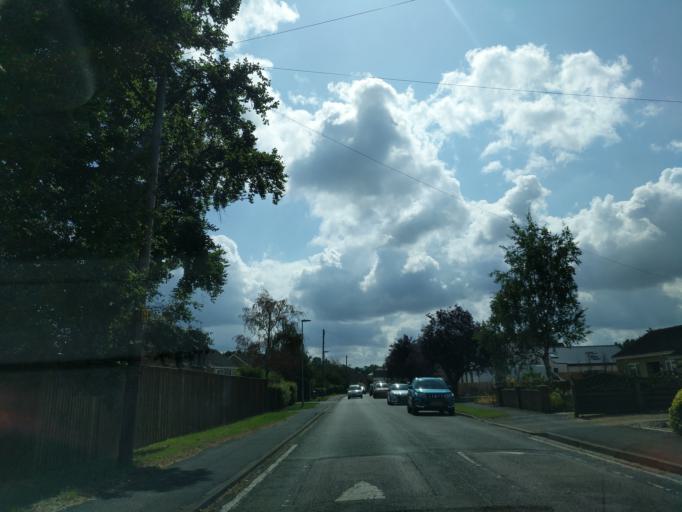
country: GB
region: England
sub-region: Cambridgeshire
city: Isleham
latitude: 52.3136
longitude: 0.3829
